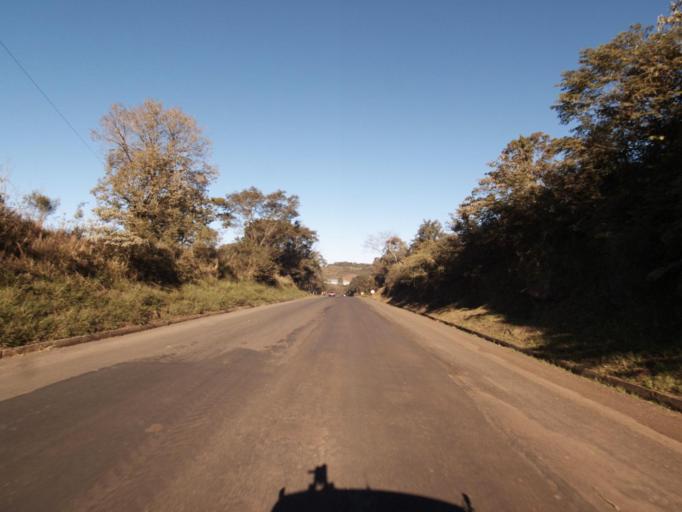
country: BR
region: Rio Grande do Sul
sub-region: Frederico Westphalen
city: Frederico Westphalen
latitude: -26.8923
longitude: -53.1869
